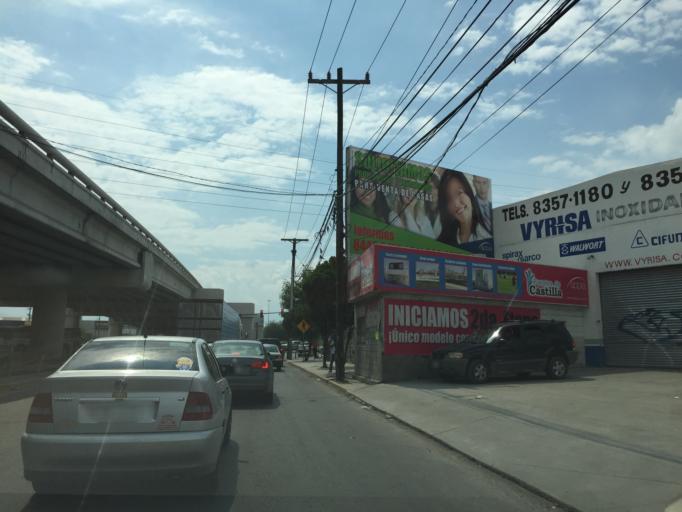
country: MX
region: Nuevo Leon
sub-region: San Nicolas de los Garza
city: San Nicolas de los Garza
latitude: 25.7685
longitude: -100.2918
